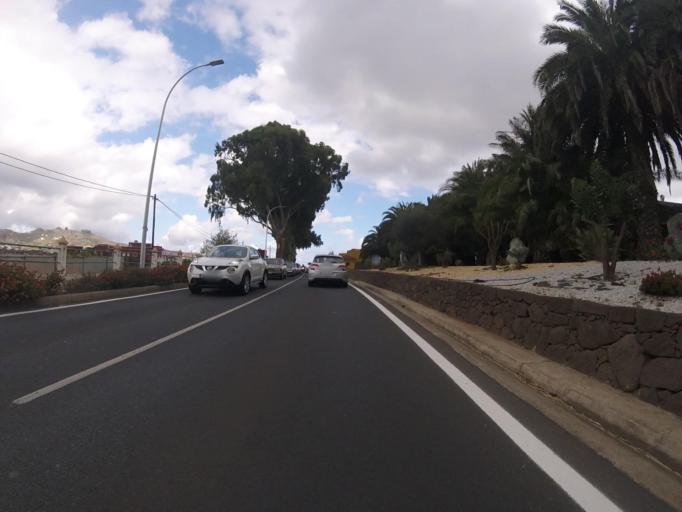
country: ES
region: Canary Islands
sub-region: Provincia de Las Palmas
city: Vega de San Mateo
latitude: 28.0143
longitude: -15.5266
